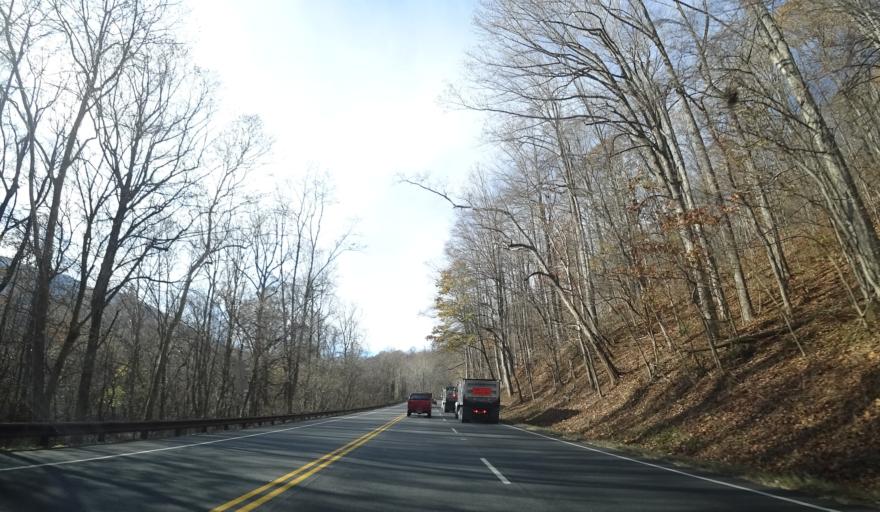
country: US
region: Virginia
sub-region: Greene County
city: Stanardsville
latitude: 38.3452
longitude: -78.5147
